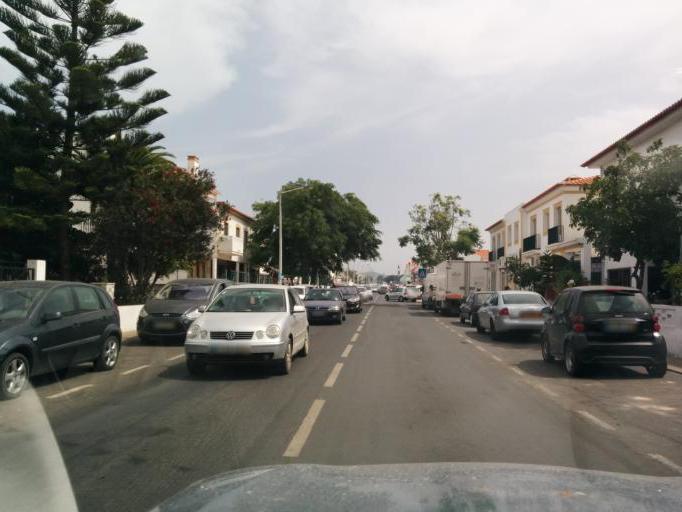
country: PT
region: Beja
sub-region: Odemira
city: Vila Nova de Milfontes
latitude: 37.7283
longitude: -8.7776
